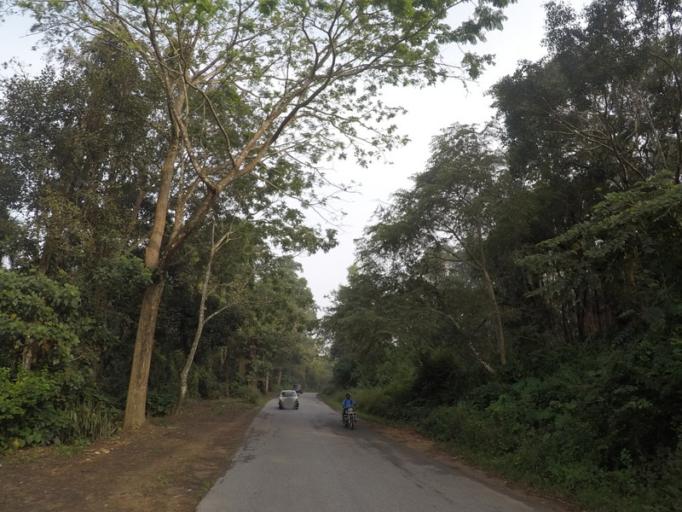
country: IN
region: Karnataka
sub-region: Chikmagalur
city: Chikmagalur
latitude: 13.2603
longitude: 75.6777
